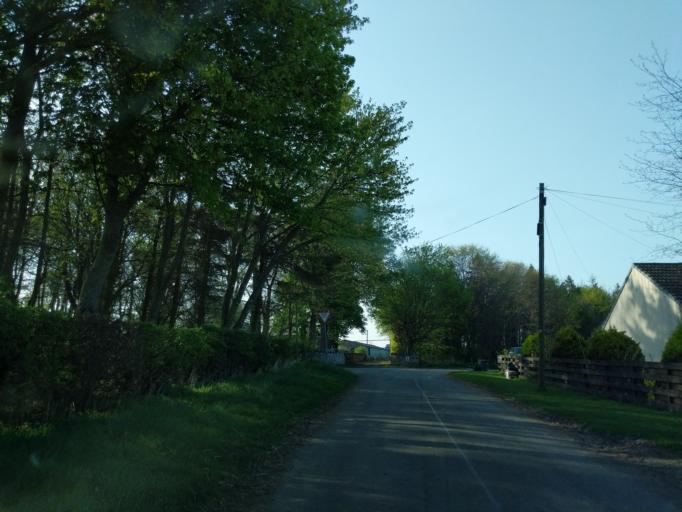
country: GB
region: Scotland
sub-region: Fife
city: Pathhead
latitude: 55.8606
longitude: -2.9466
